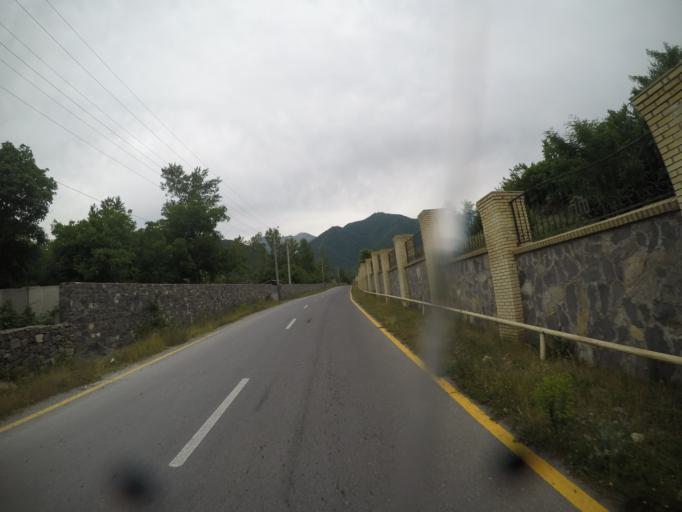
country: AZ
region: Shaki City
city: Sheki
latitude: 41.2467
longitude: 47.2011
